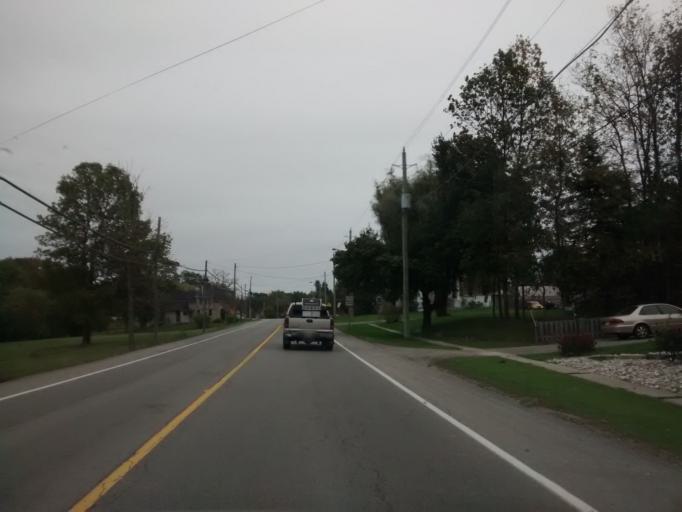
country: CA
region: Ontario
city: Welland
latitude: 42.8927
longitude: -79.6294
